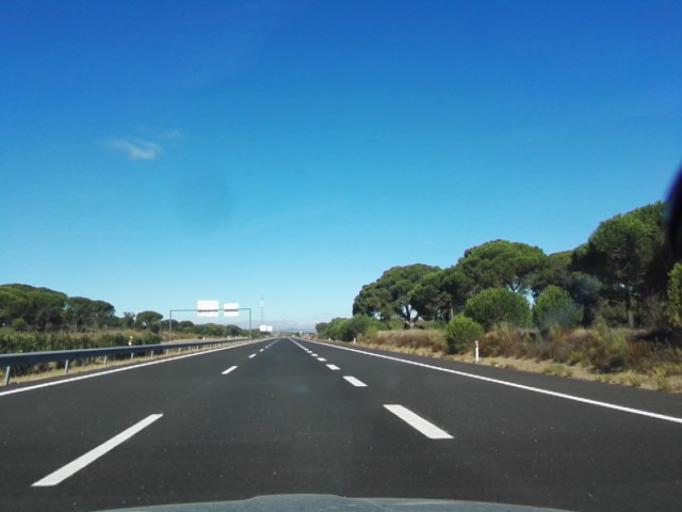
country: PT
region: Santarem
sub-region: Benavente
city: Benavente
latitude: 38.9112
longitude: -8.7910
